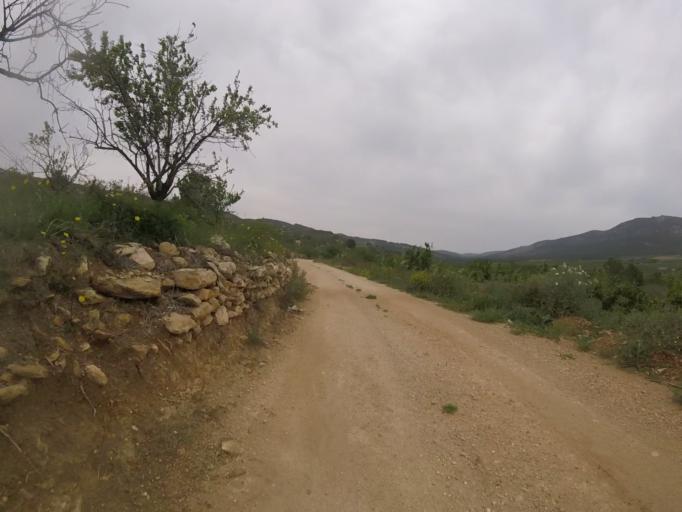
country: ES
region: Valencia
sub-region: Provincia de Castello
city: Alcala de Xivert
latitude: 40.2858
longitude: 0.2573
